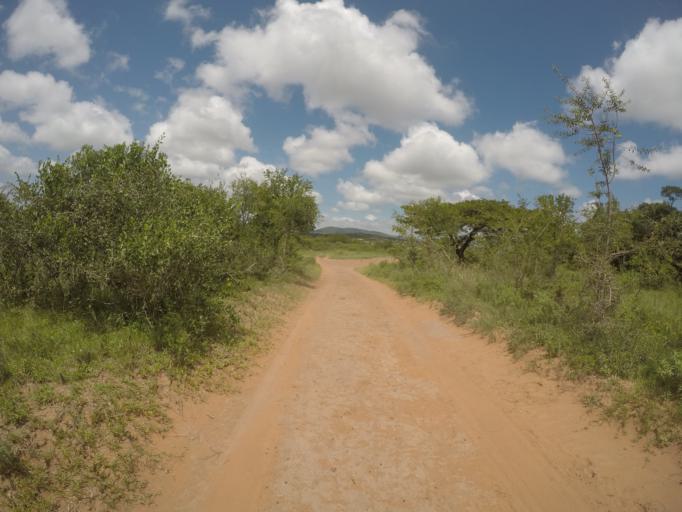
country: ZA
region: KwaZulu-Natal
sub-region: uThungulu District Municipality
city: Empangeni
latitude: -28.5871
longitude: 31.8325
